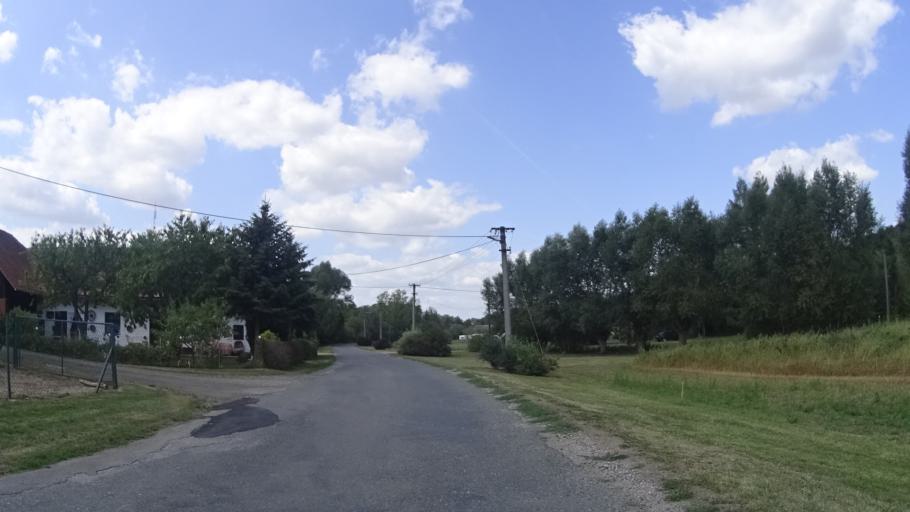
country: CZ
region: Kralovehradecky
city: Kopidlno
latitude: 50.3833
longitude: 15.3026
